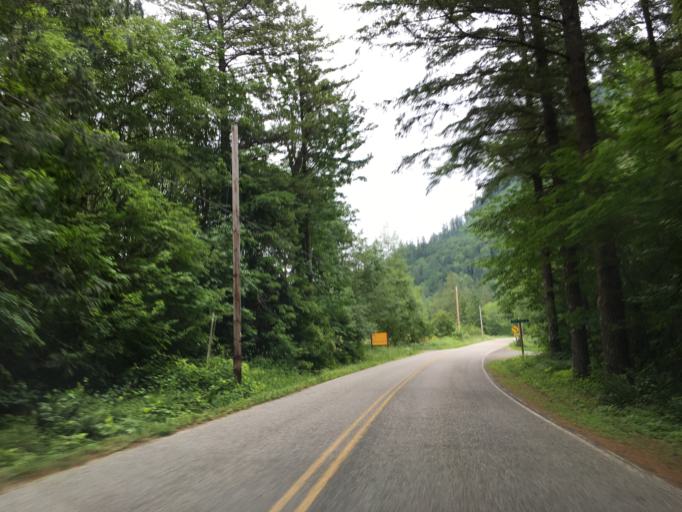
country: US
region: Washington
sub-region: Whatcom County
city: Peaceful Valley
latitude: 48.9856
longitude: -122.0739
